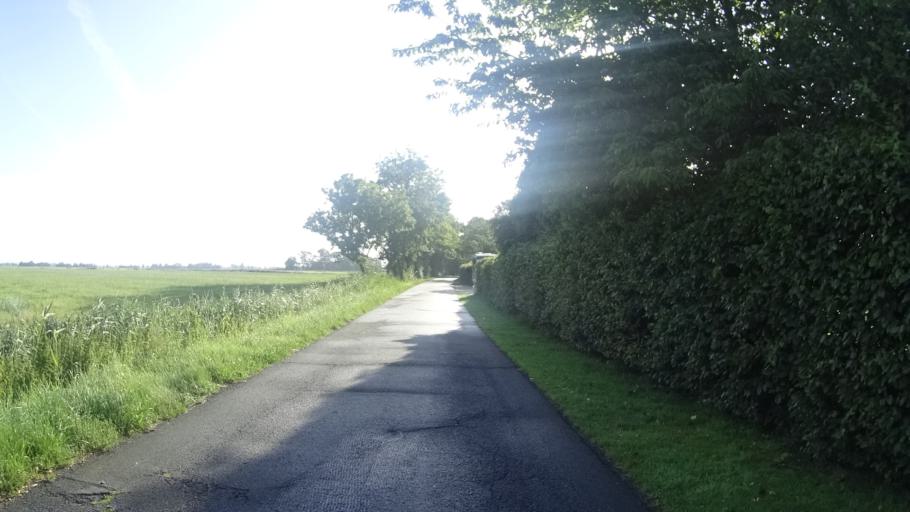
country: DE
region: Lower Saxony
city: Nordenham
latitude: 53.4973
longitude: 8.4219
